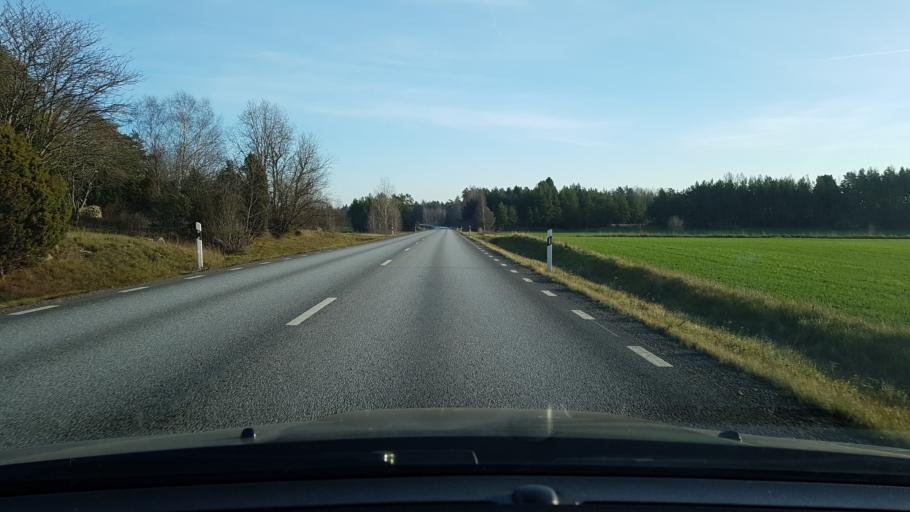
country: SE
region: Stockholm
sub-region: Vallentuna Kommun
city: Vallentuna
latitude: 59.7484
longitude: 18.0713
